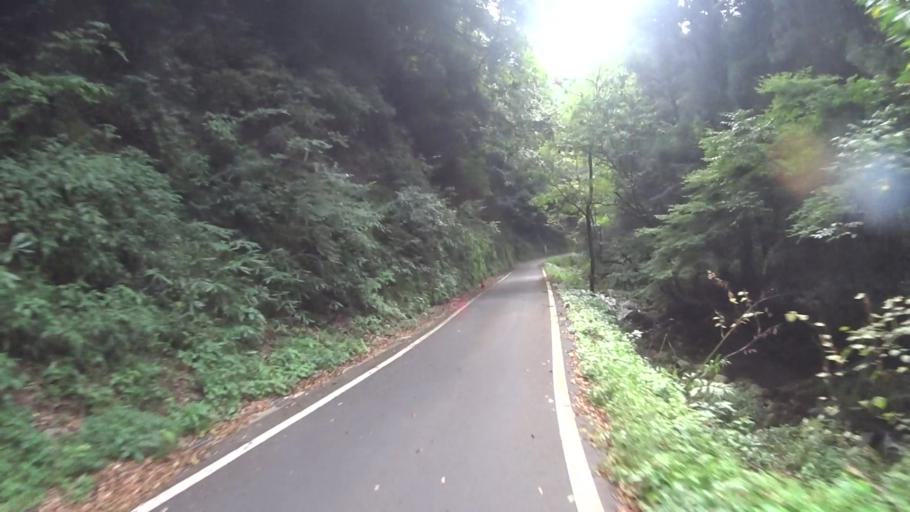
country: JP
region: Kyoto
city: Miyazu
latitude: 35.6112
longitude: 135.2050
